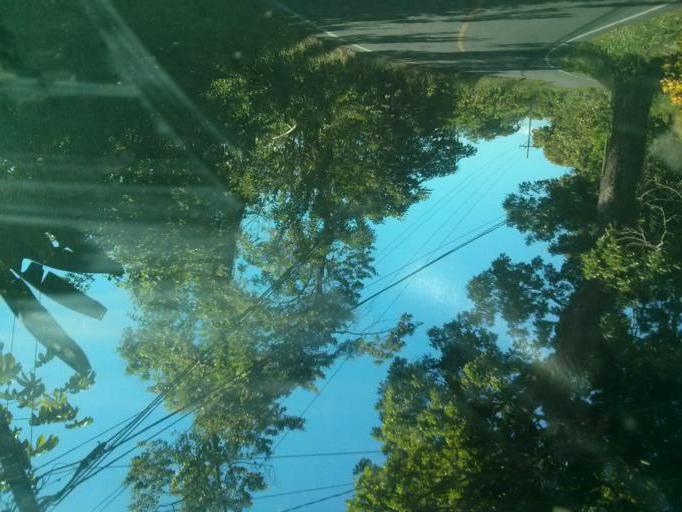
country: CR
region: Puntarenas
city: Paquera
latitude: 9.8104
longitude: -84.9399
